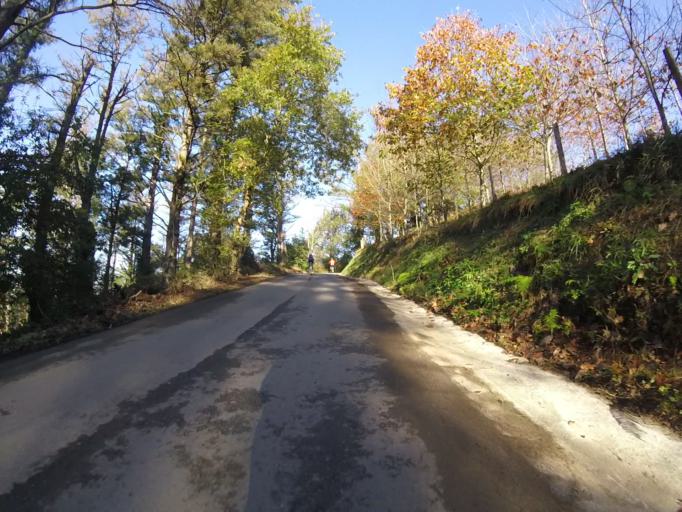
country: ES
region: Basque Country
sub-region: Provincia de Guipuzcoa
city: Usurbil
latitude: 43.2794
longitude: -2.0701
